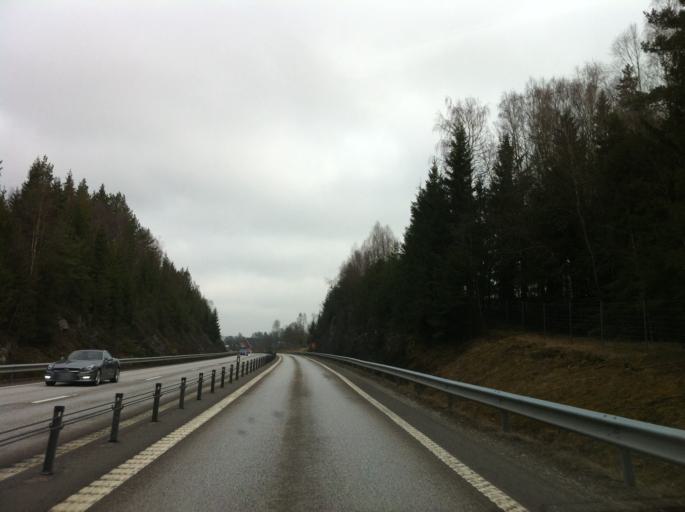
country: SE
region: Vaestra Goetaland
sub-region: Boras Kommun
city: Dalsjofors
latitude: 57.7565
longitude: 13.1048
